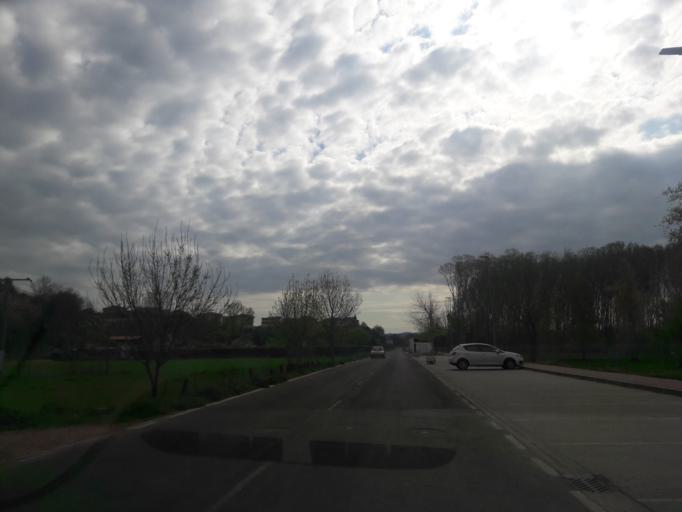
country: ES
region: Castille and Leon
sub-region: Provincia de Salamanca
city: Ciudad Rodrigo
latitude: 40.5937
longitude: -6.5305
